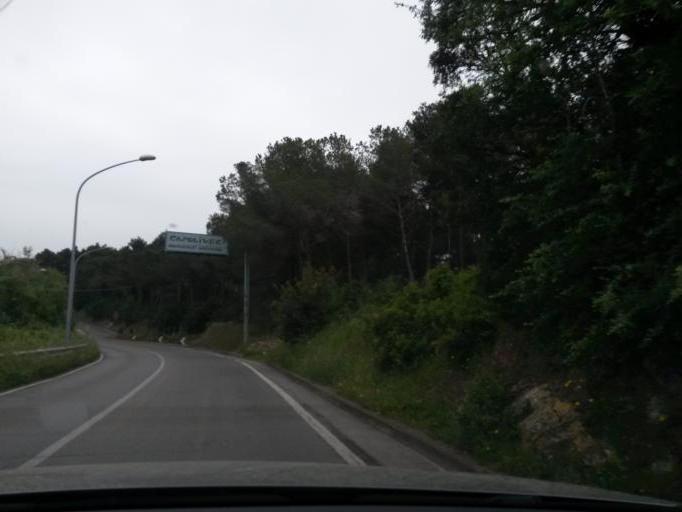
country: IT
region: Tuscany
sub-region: Provincia di Livorno
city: Capoliveri
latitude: 42.7468
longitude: 10.3721
